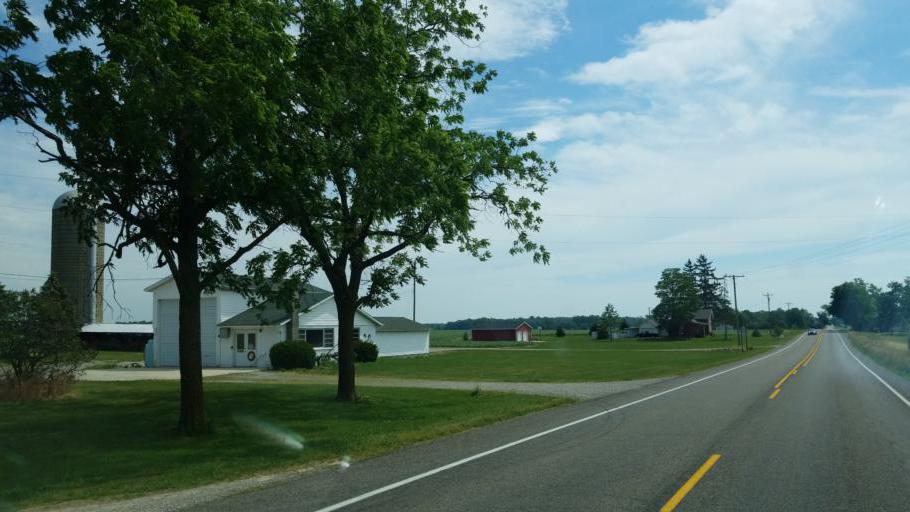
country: US
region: Michigan
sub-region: Eaton County
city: Charlotte
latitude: 42.6260
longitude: -84.8356
